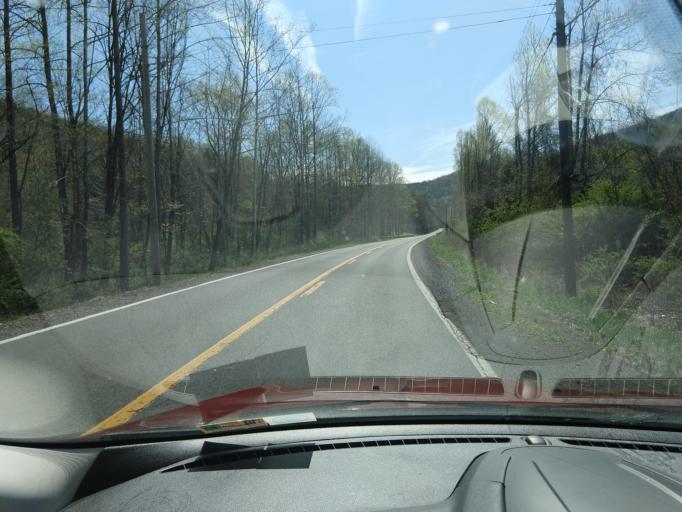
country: US
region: West Virginia
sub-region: Greenbrier County
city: Alderson
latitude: 37.7244
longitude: -80.6299
